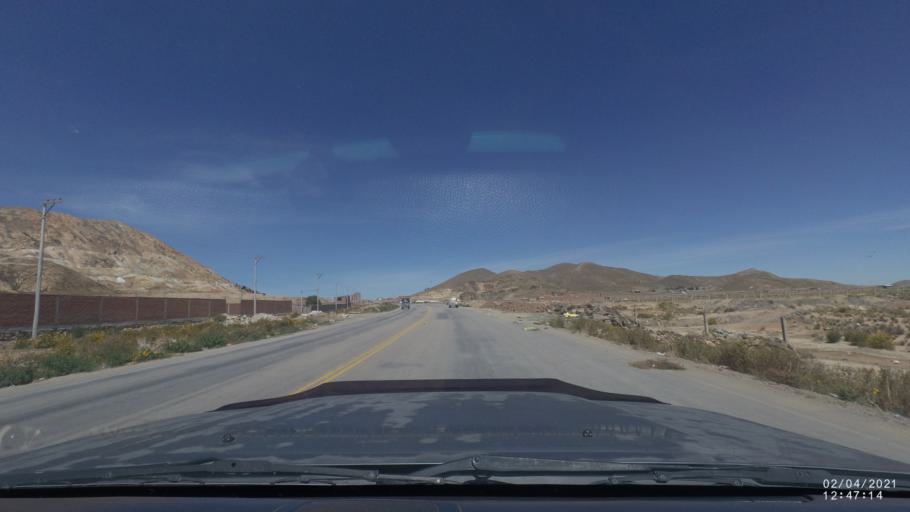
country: BO
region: Oruro
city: Oruro
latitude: -17.9507
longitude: -67.1444
